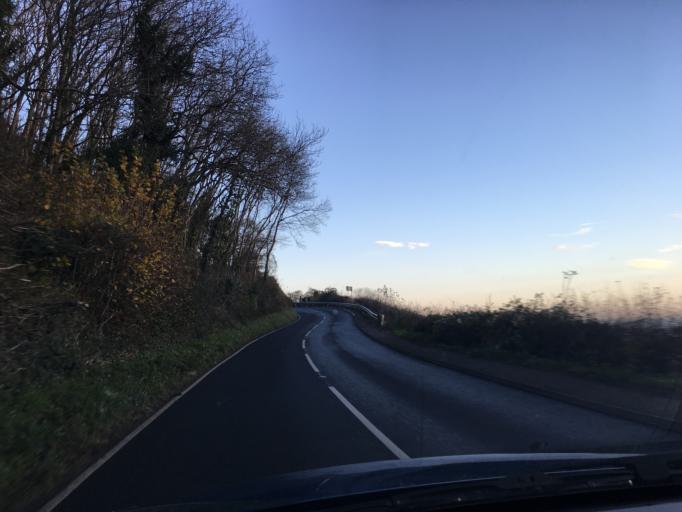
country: GB
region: England
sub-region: Isle of Wight
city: Ventnor
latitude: 50.6078
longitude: -1.1879
